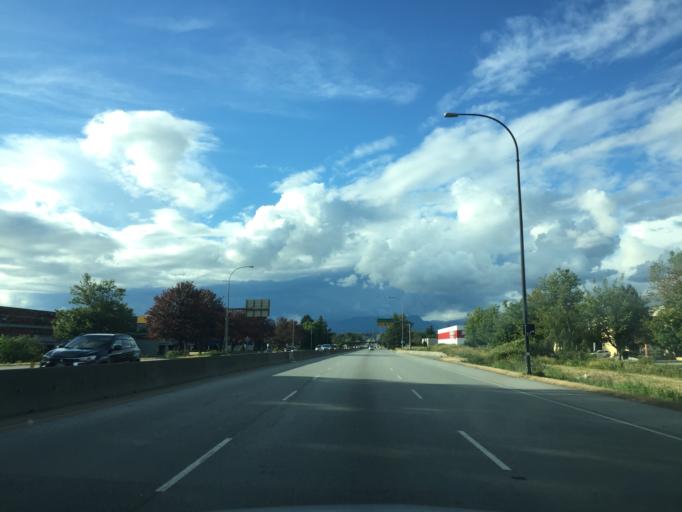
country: CA
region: British Columbia
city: Richmond
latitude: 49.1859
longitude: -123.0773
